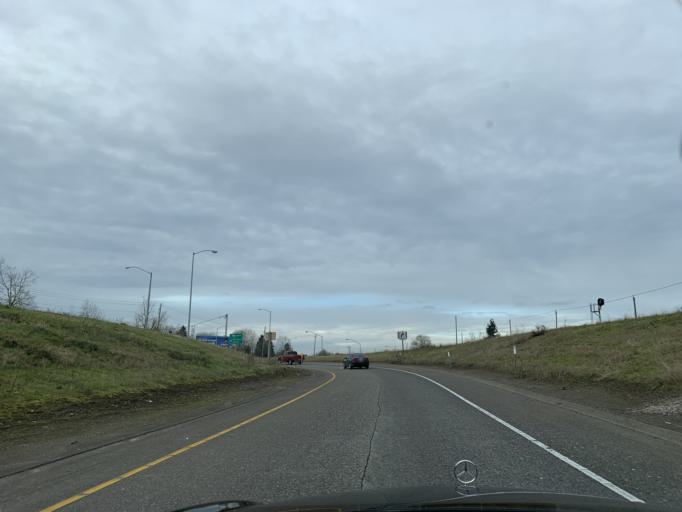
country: US
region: Oregon
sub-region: Multnomah County
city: Lents
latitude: 45.5617
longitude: -122.5642
